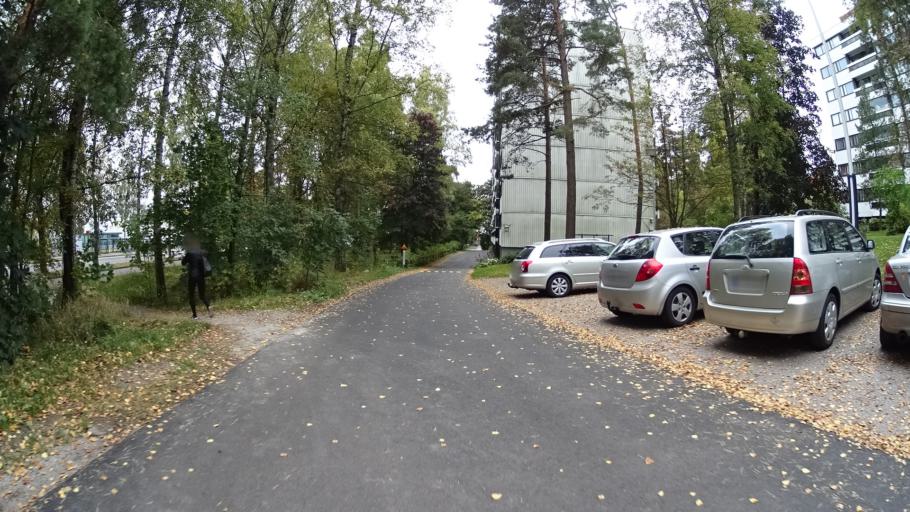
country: FI
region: Uusimaa
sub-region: Helsinki
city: Vantaa
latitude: 60.2262
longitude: 25.0736
